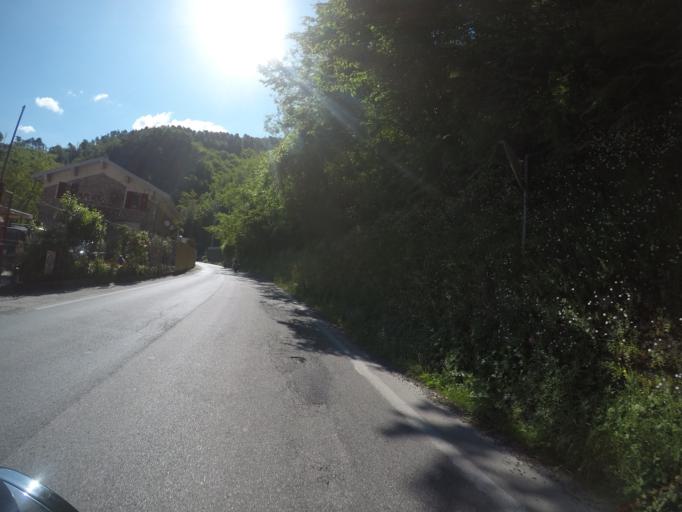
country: IT
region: Tuscany
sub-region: Provincia di Massa-Carrara
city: Montignoso
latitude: 44.0456
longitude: 10.1521
